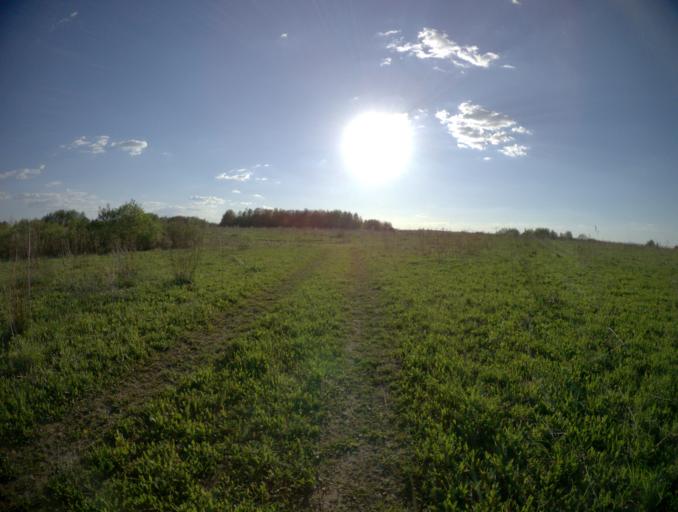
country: RU
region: Ivanovo
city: Gavrilov Posad
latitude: 56.3814
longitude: 40.1278
